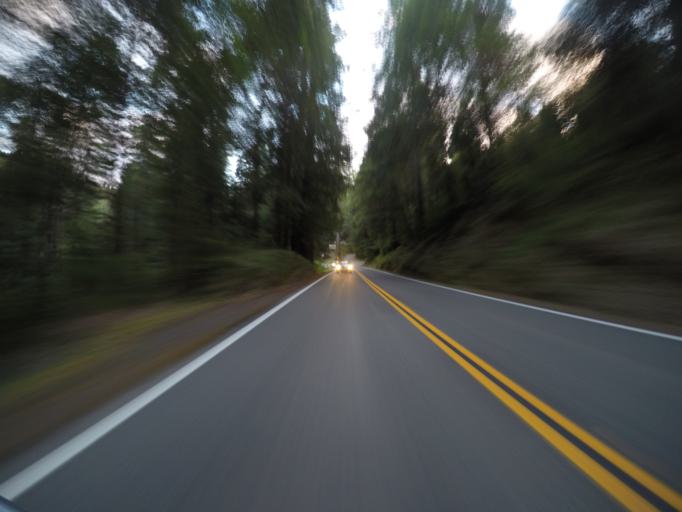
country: US
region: California
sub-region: Humboldt County
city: Redway
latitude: 40.0291
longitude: -123.7940
